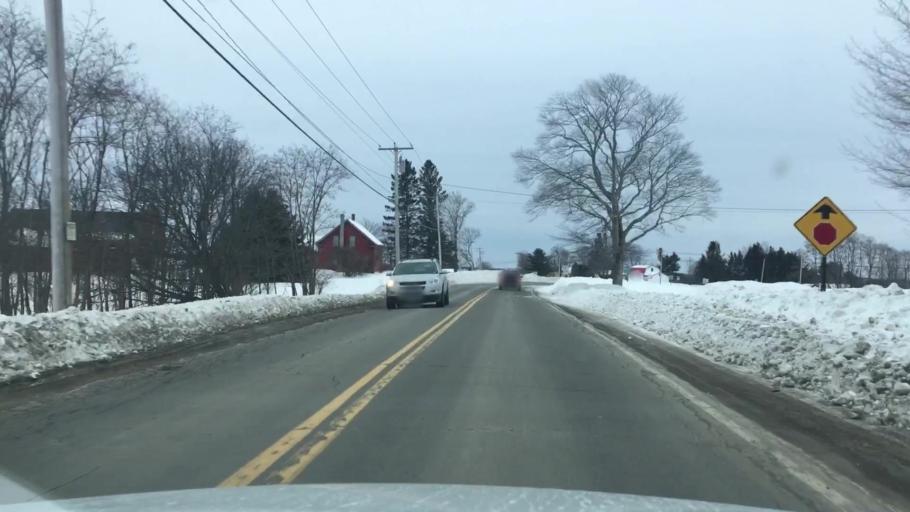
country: US
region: Maine
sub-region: Penobscot County
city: Charleston
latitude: 45.0309
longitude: -69.0314
